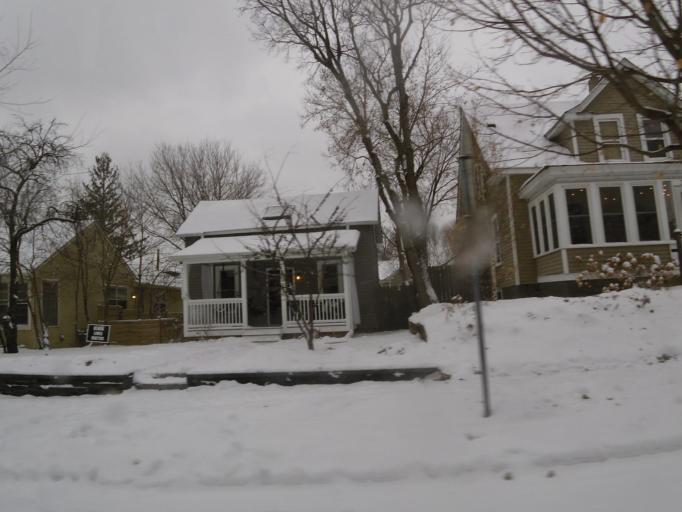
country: US
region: Minnesota
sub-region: Hennepin County
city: Minneapolis
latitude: 44.9370
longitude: -93.2639
